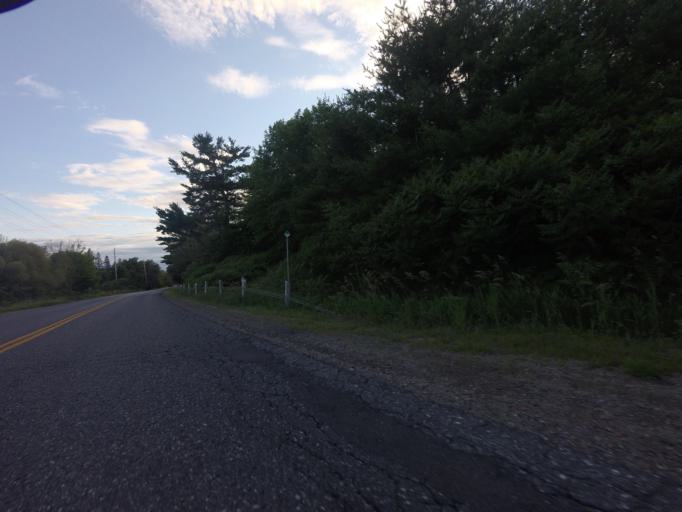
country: CA
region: Ontario
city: Renfrew
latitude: 45.3687
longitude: -76.6118
